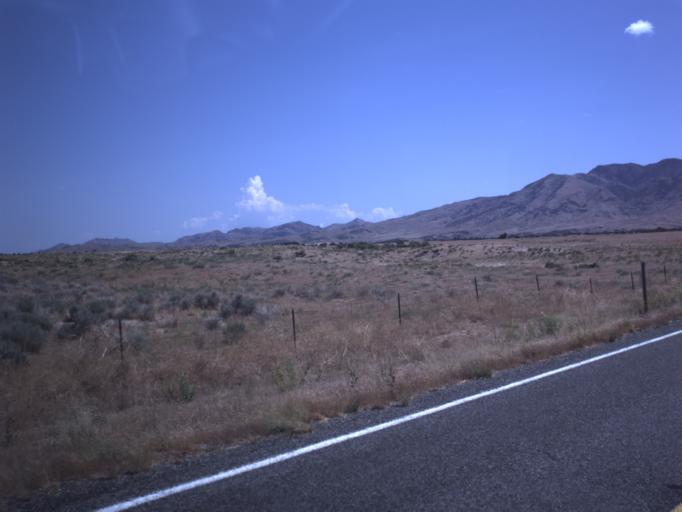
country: US
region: Utah
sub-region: Millard County
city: Delta
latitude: 39.3548
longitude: -112.3828
